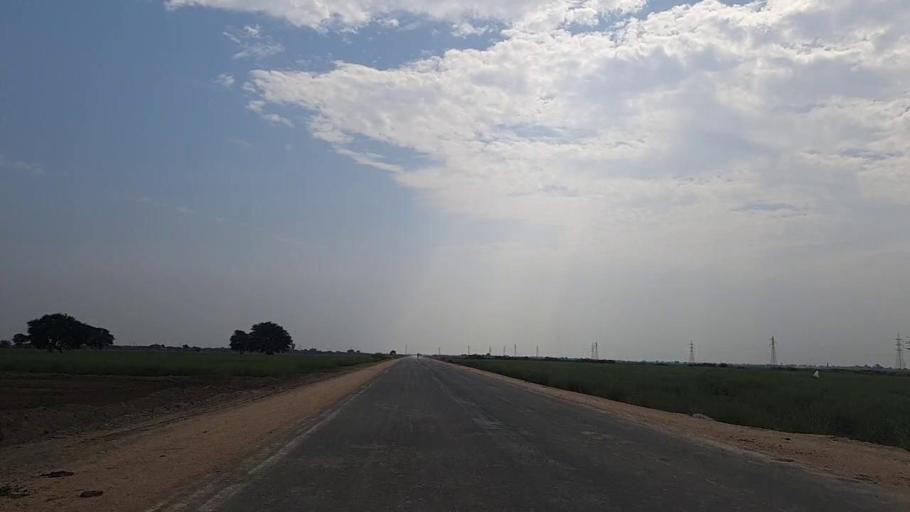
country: PK
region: Sindh
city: Naukot
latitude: 24.9676
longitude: 69.2827
